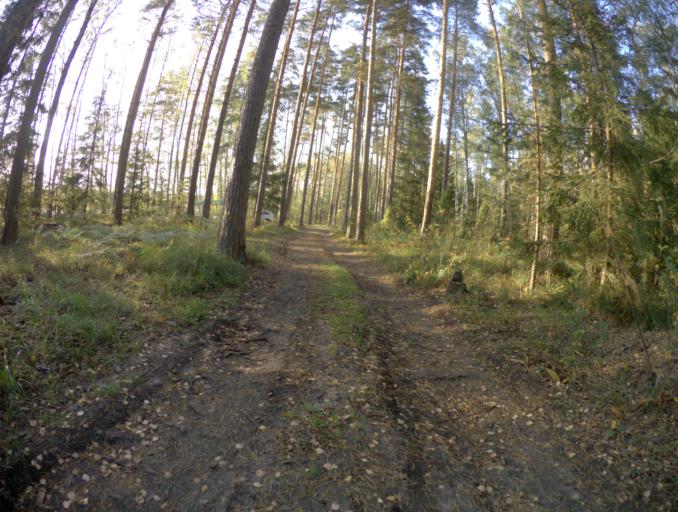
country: RU
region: Moskovskaya
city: Misheronskiy
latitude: 55.6283
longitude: 39.7188
